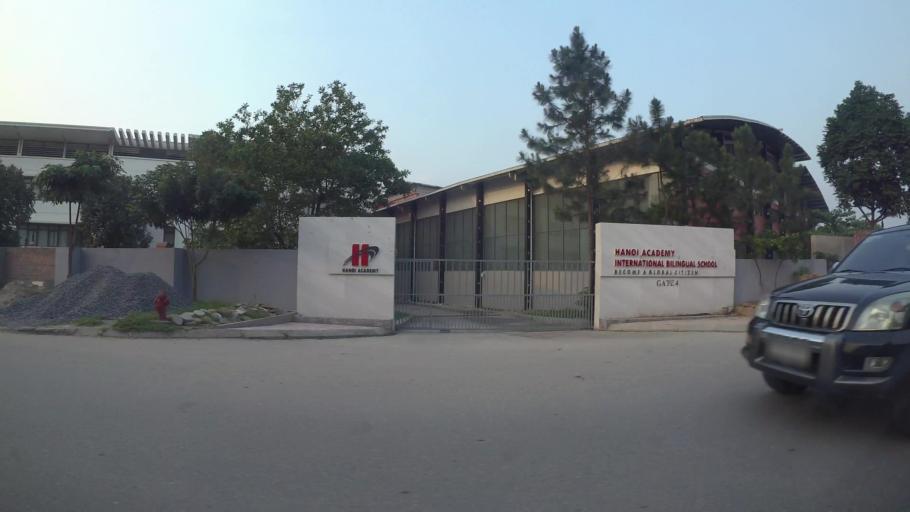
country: VN
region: Ha Noi
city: Tay Ho
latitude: 21.0727
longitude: 105.8031
